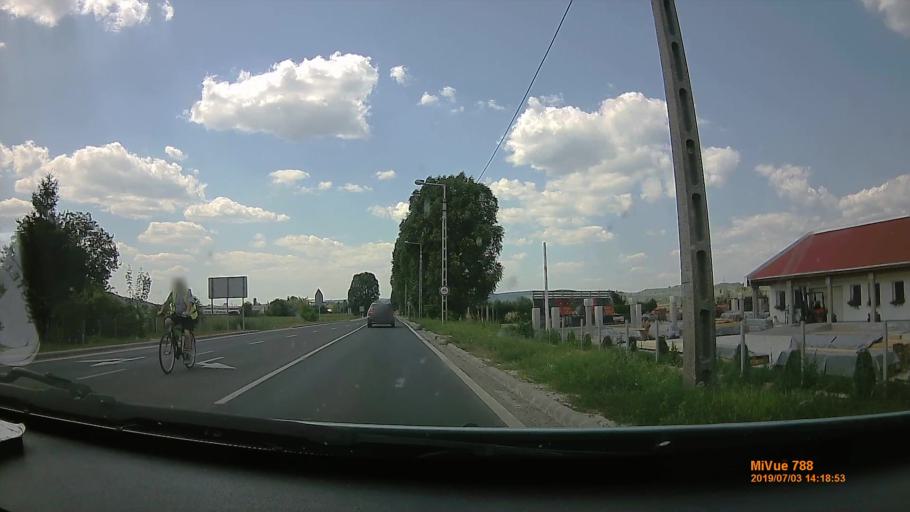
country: HU
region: Borsod-Abauj-Zemplen
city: Kazincbarcika
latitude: 48.2615
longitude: 20.6168
